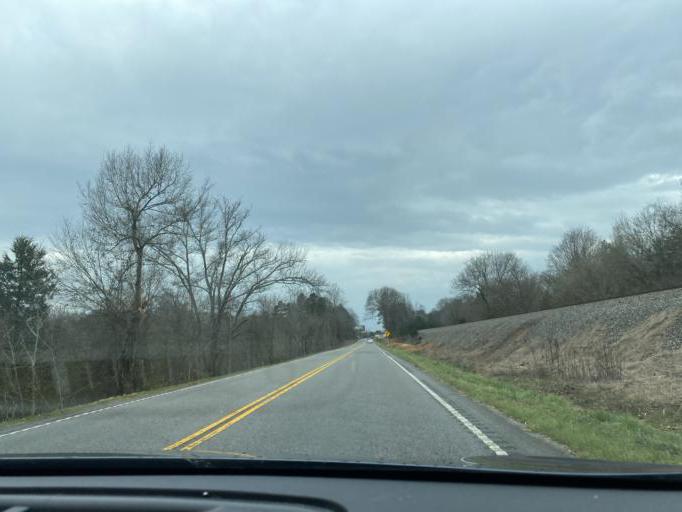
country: US
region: South Carolina
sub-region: Spartanburg County
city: Cowpens
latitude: 35.0189
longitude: -81.7213
